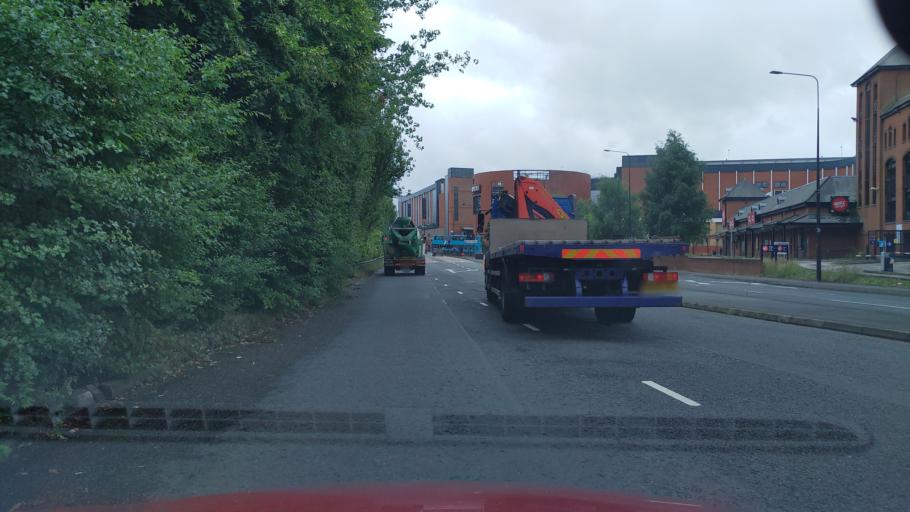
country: GB
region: England
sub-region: Borough of Wigan
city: Ince-in-Makerfield
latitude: 53.5485
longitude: -2.6272
